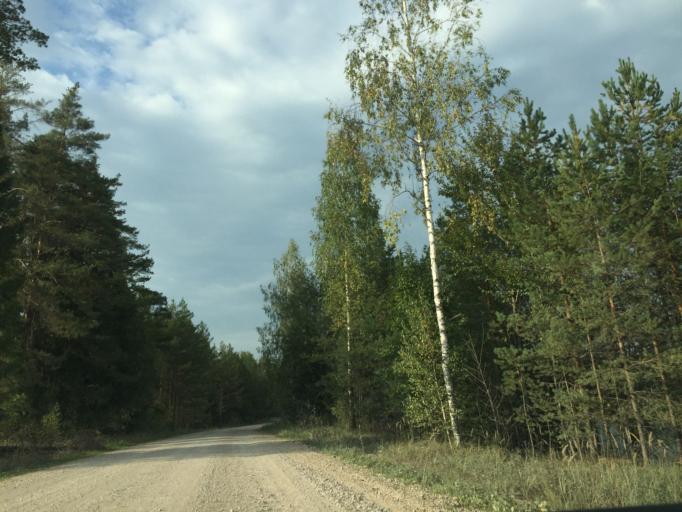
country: LV
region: Baldone
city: Baldone
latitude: 56.7908
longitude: 24.4409
